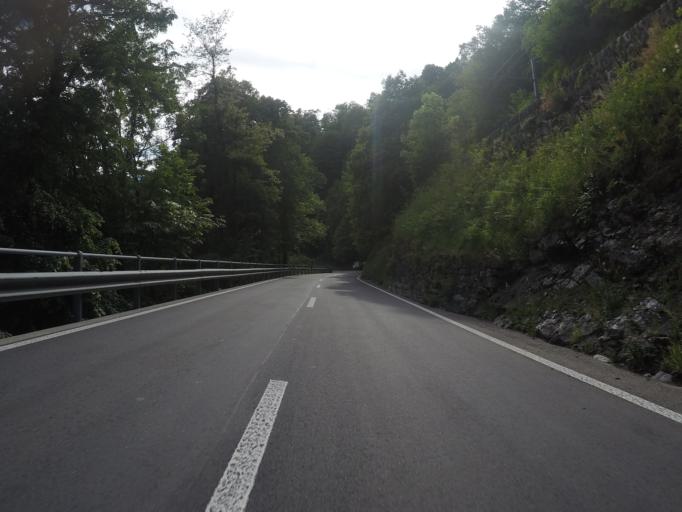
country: CH
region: Ticino
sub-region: Locarno District
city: Brissago
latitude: 46.1624
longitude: 8.6378
